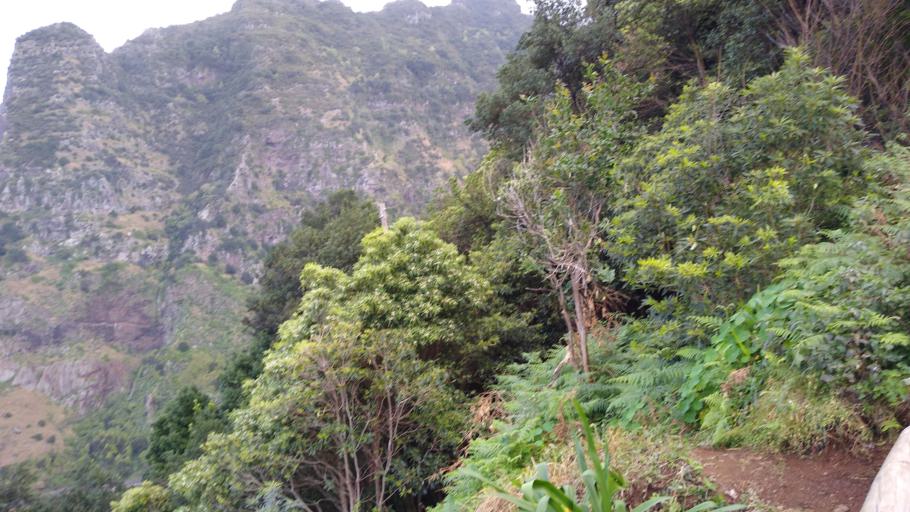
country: PT
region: Madeira
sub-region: Sao Vicente
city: Sao Vicente
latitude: 32.8228
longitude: -16.9737
